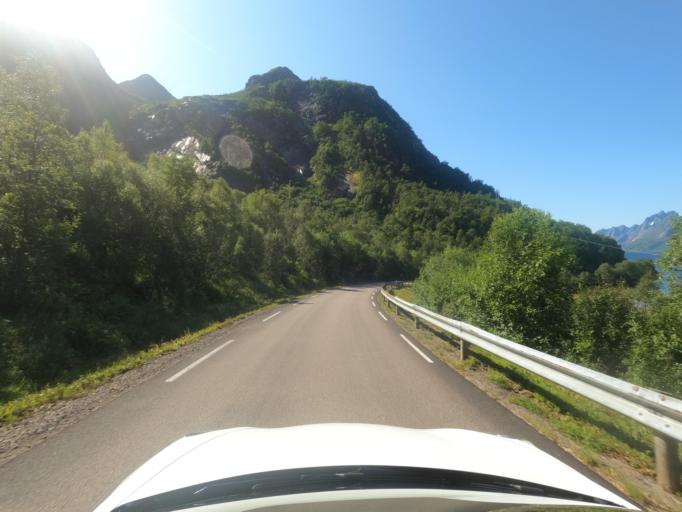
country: NO
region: Nordland
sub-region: Hadsel
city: Stokmarknes
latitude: 68.3398
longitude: 15.0475
